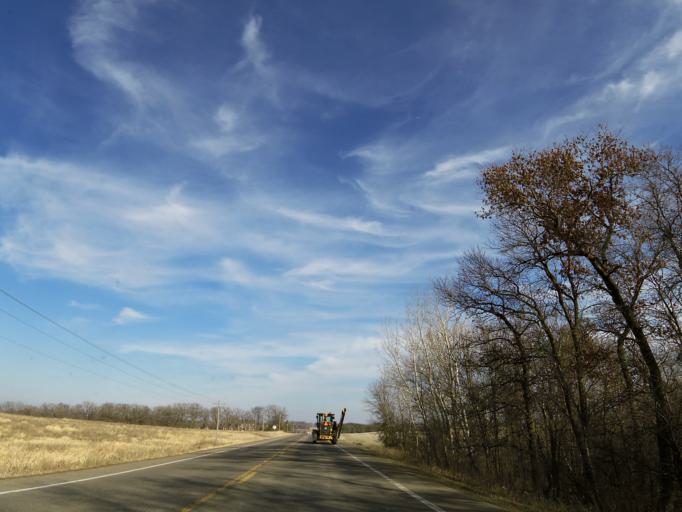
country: US
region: Minnesota
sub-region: Rice County
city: Northfield
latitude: 44.5441
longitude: -93.2221
